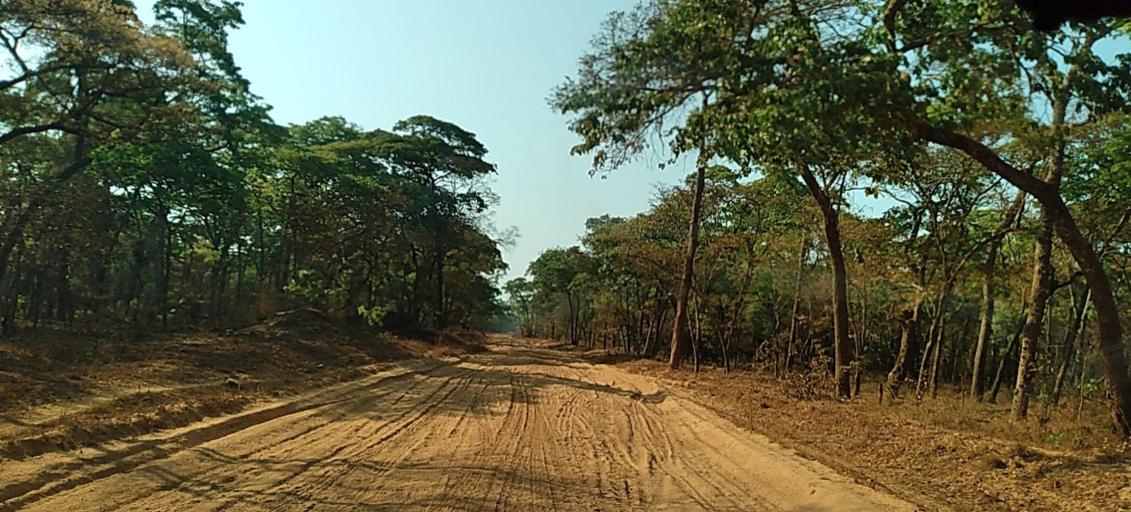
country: ZM
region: North-Western
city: Kasempa
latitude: -13.6325
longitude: 25.9897
